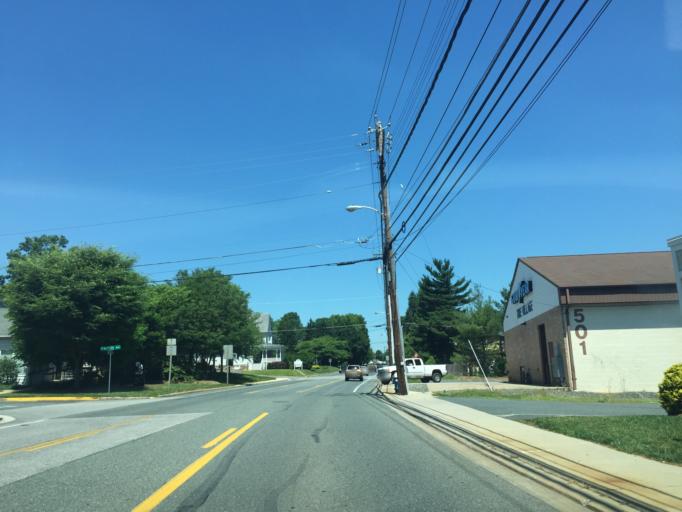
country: US
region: Maryland
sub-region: Harford County
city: North Bel Air
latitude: 39.5405
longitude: -76.3569
